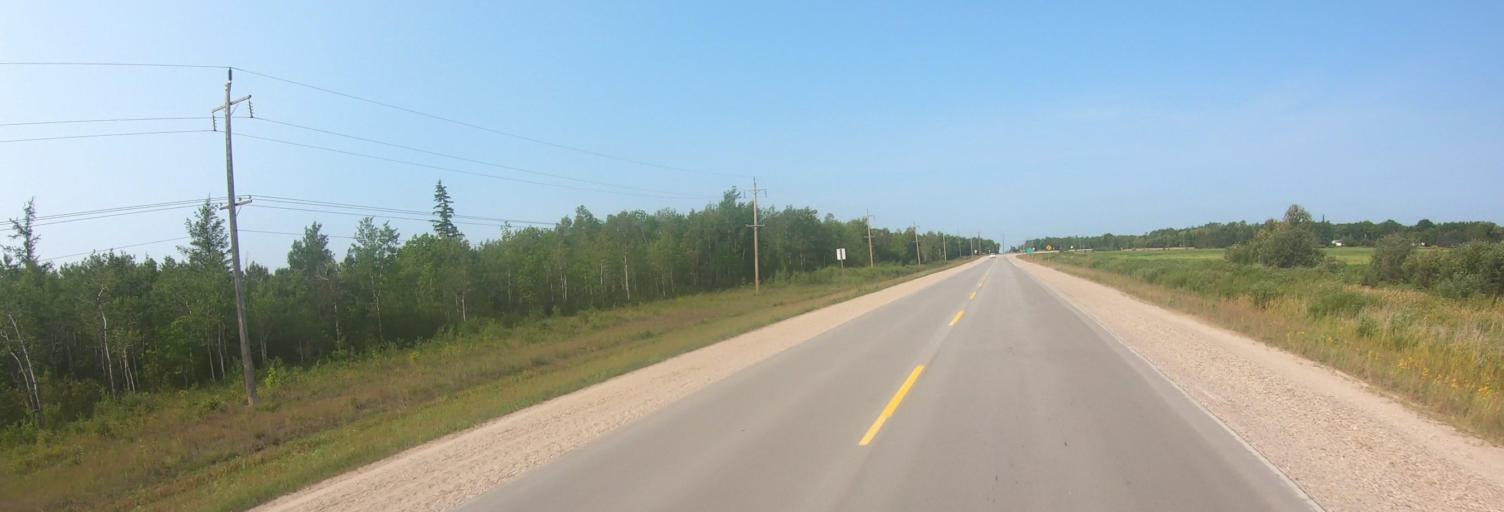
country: US
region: Minnesota
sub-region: Roseau County
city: Roseau
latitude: 49.0896
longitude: -95.9713
